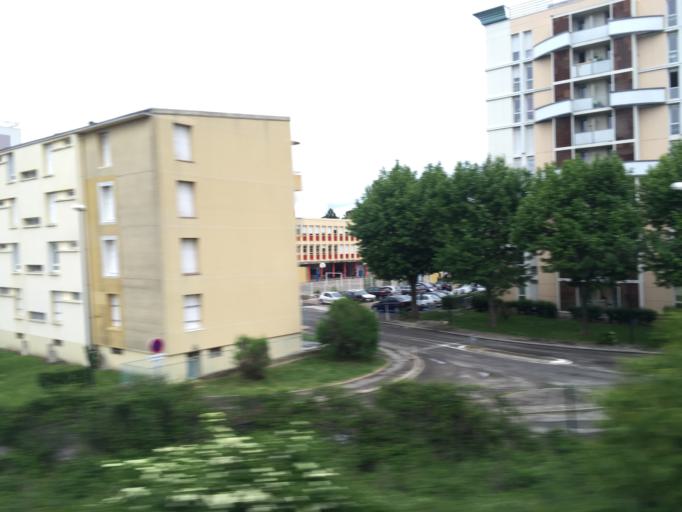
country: FR
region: Rhone-Alpes
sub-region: Departement de la Drome
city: Montelimar
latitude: 44.5485
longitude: 4.7412
